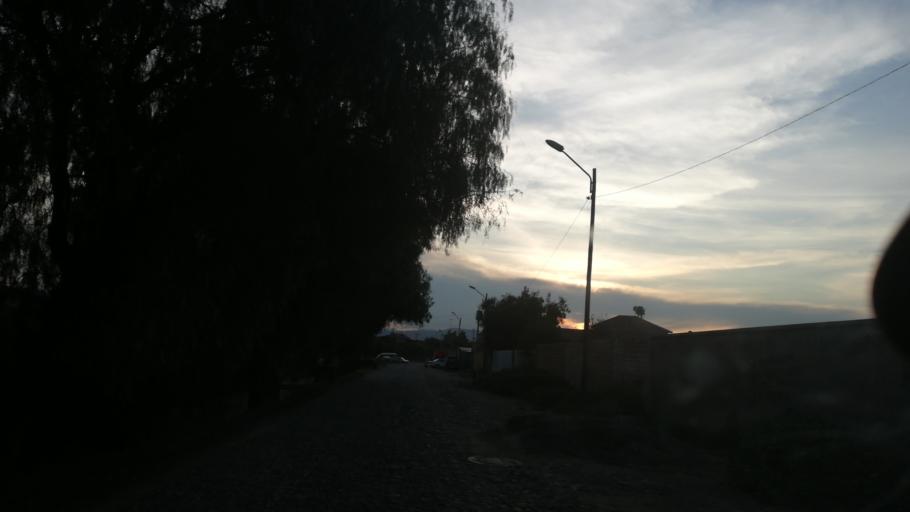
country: BO
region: Cochabamba
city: Cochabamba
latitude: -17.3818
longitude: -66.2038
